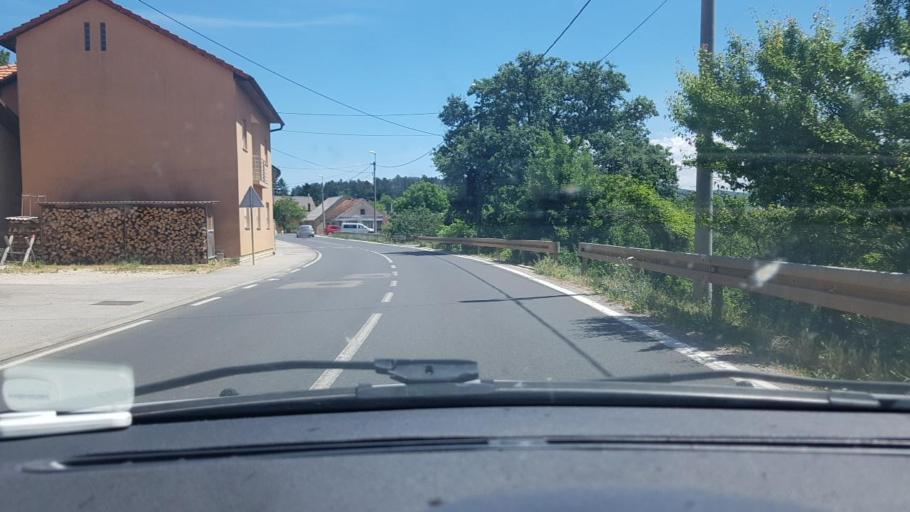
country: HR
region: Licko-Senjska
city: Otocac
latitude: 44.8705
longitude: 15.2249
